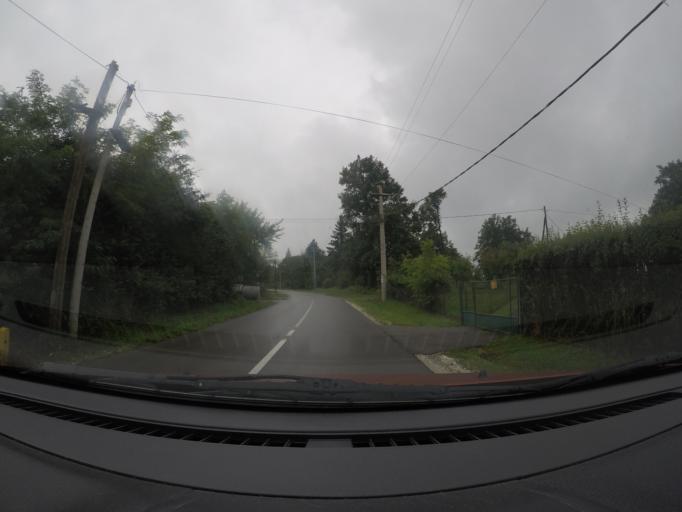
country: RS
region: Central Serbia
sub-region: Belgrade
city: Sopot
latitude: 44.5439
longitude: 20.5409
